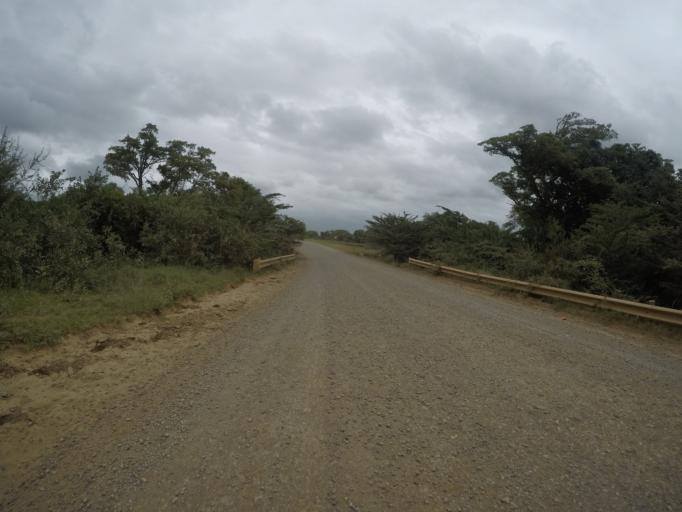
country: ZA
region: KwaZulu-Natal
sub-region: uThungulu District Municipality
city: Empangeni
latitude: -28.5890
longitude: 31.8429
